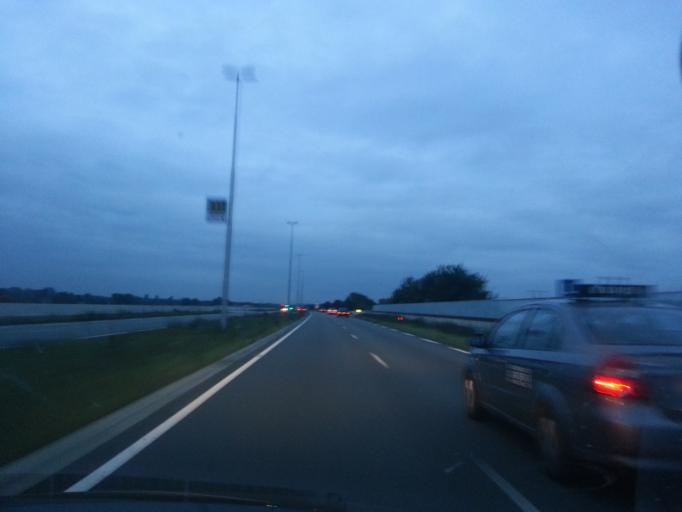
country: NL
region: North Brabant
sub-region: Gemeente Tilburg
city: Tilburg
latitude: 51.5680
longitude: 5.1297
